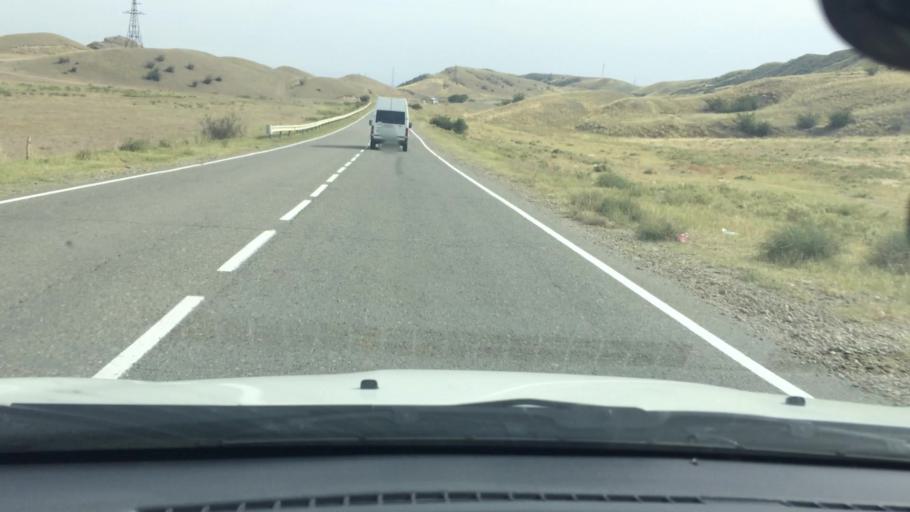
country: GE
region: Kvemo Kartli
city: Rust'avi
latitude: 41.5344
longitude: 44.9806
